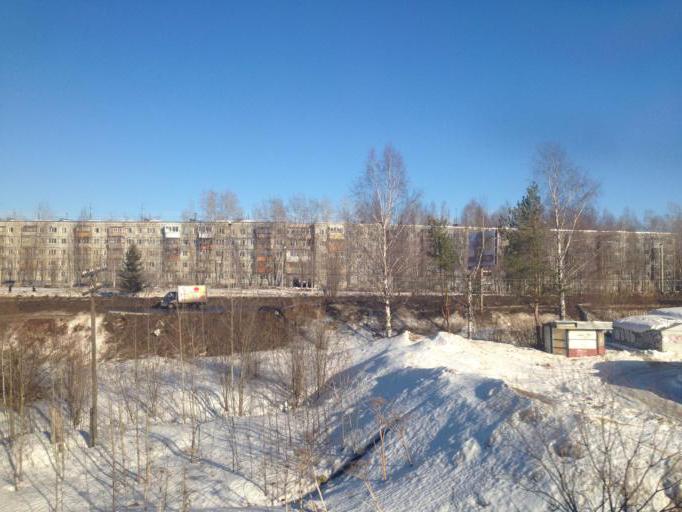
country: RU
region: Komi Republic
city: Ezhva
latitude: 61.7931
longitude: 50.7387
